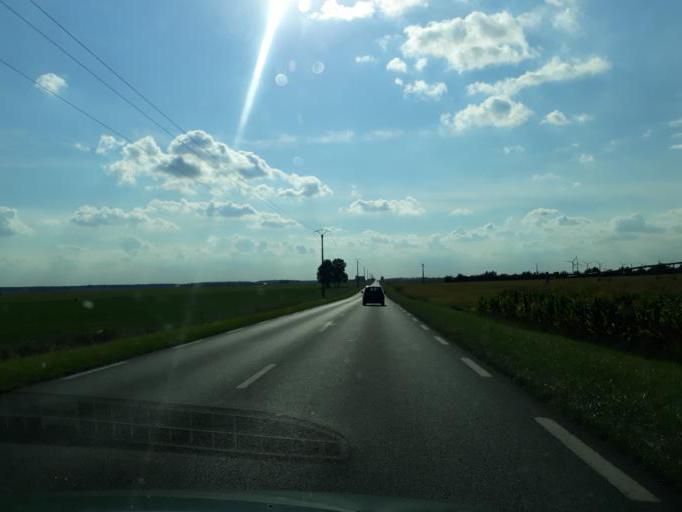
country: FR
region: Centre
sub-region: Departement du Loir-et-Cher
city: Ouzouer-le-Marche
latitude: 47.9042
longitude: 1.4177
